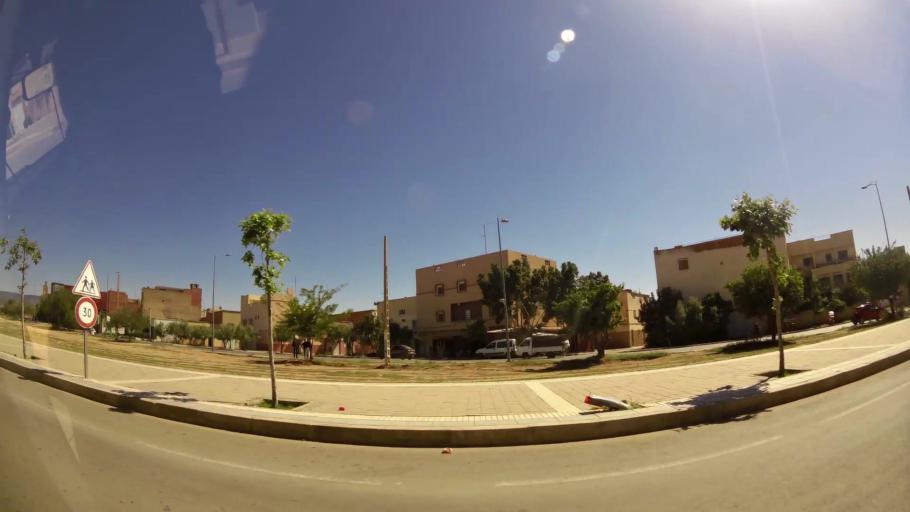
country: MA
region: Oriental
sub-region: Oujda-Angad
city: Oujda
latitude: 34.6676
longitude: -1.8713
